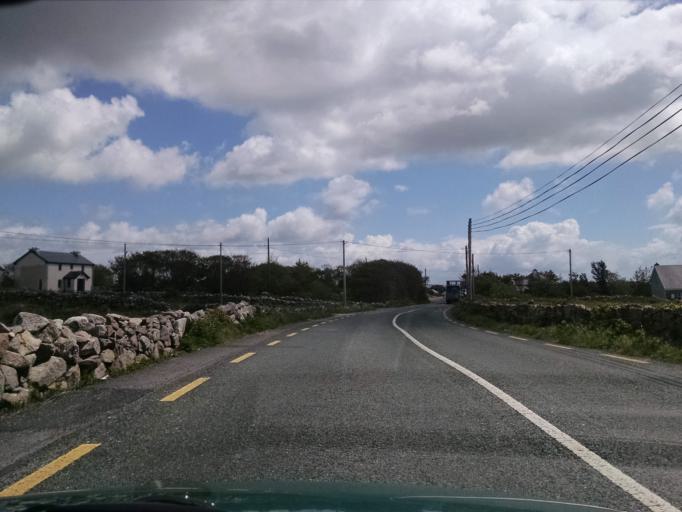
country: IE
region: Connaught
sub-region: County Galway
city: Oughterard
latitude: 53.3138
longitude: -9.6147
